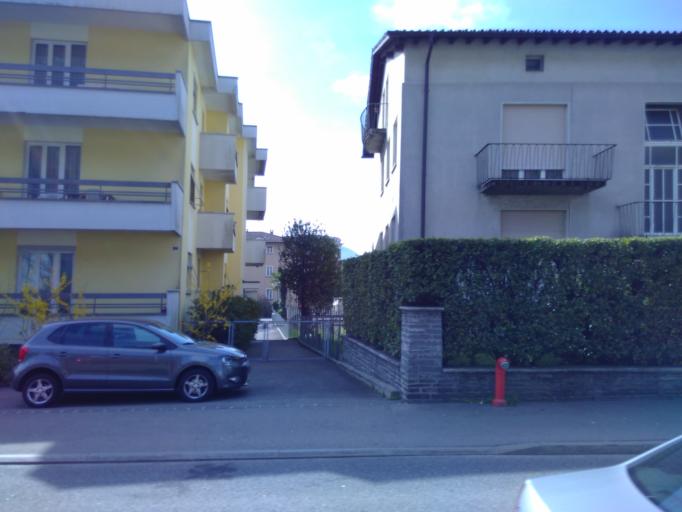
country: CH
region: Ticino
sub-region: Locarno District
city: Ascona
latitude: 46.1691
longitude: 8.7797
